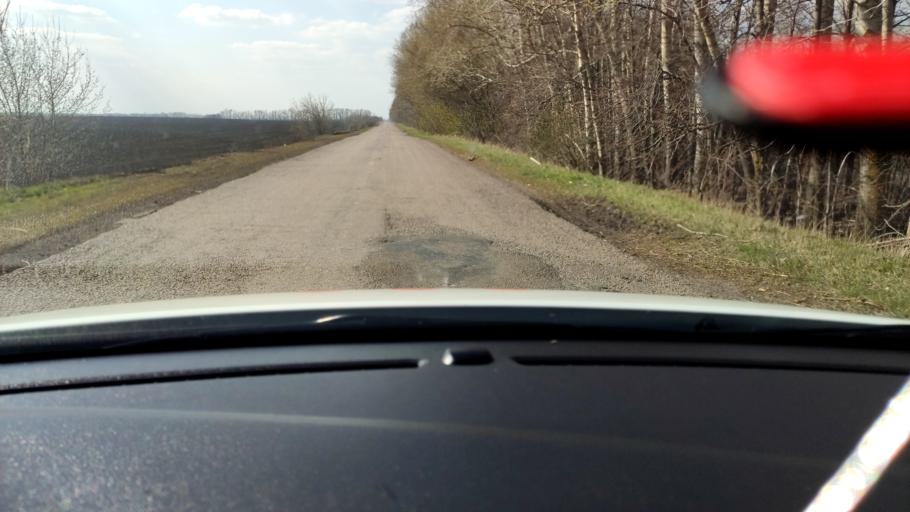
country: RU
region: Voronezj
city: Uryv-Pokrovka
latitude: 51.1261
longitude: 39.1150
